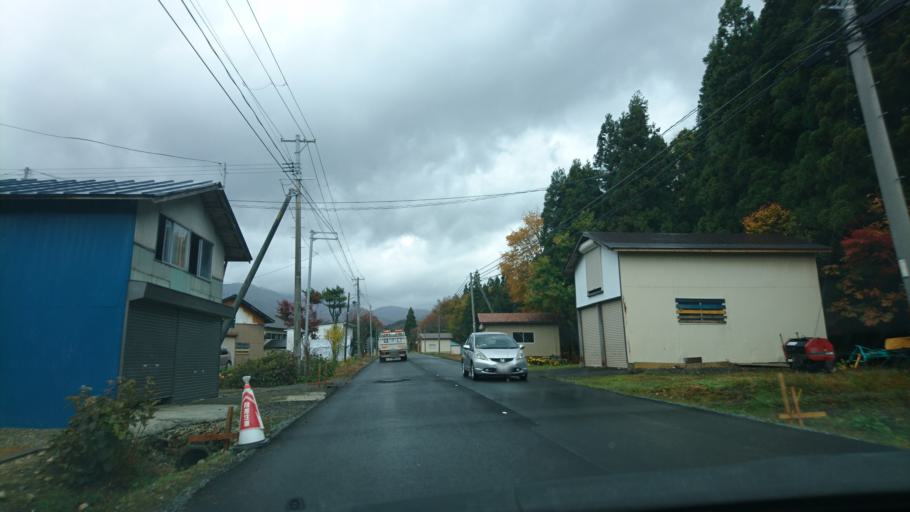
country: JP
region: Iwate
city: Shizukuishi
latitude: 39.5192
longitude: 140.8288
